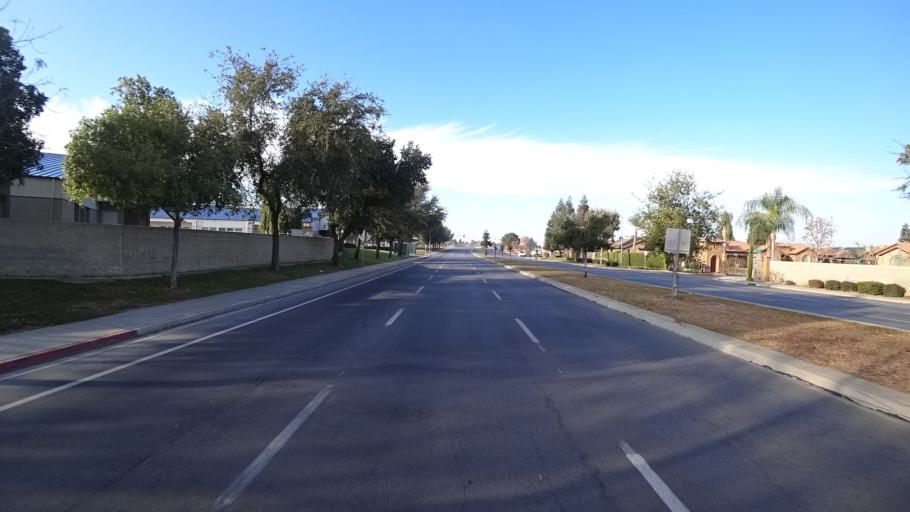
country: US
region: California
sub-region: Kern County
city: Greenacres
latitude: 35.3997
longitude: -119.0984
